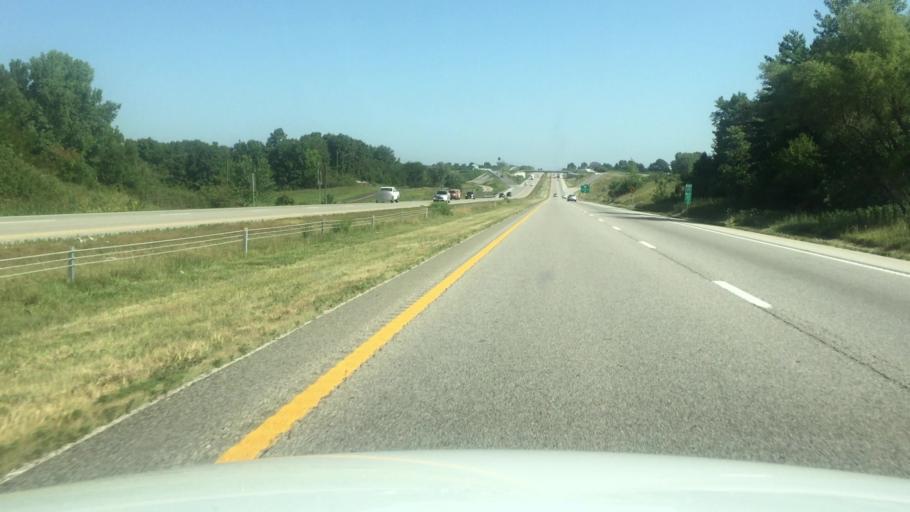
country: US
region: Kansas
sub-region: Doniphan County
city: Elwood
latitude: 39.5919
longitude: -94.7888
